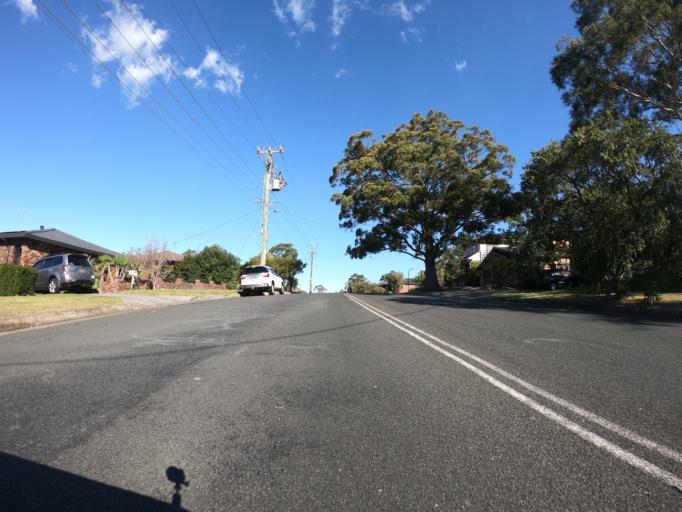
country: AU
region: New South Wales
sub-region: Wollongong
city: Mount Keira
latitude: -34.4206
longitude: 150.8554
